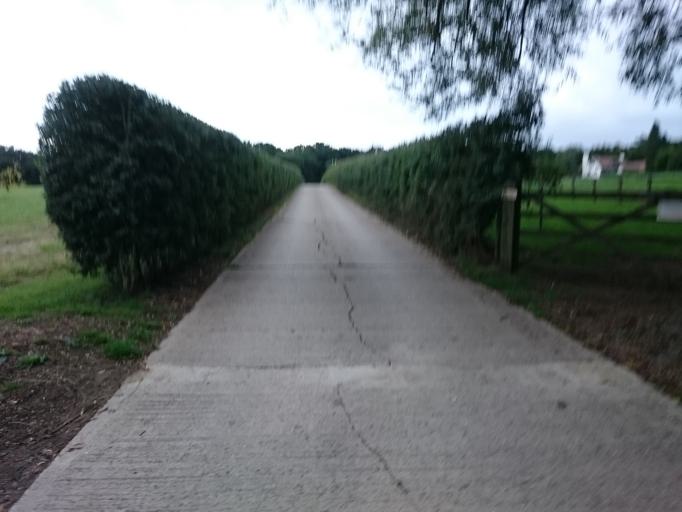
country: GB
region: England
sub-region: Oxfordshire
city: Boars Hill
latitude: 51.7211
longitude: -1.2757
